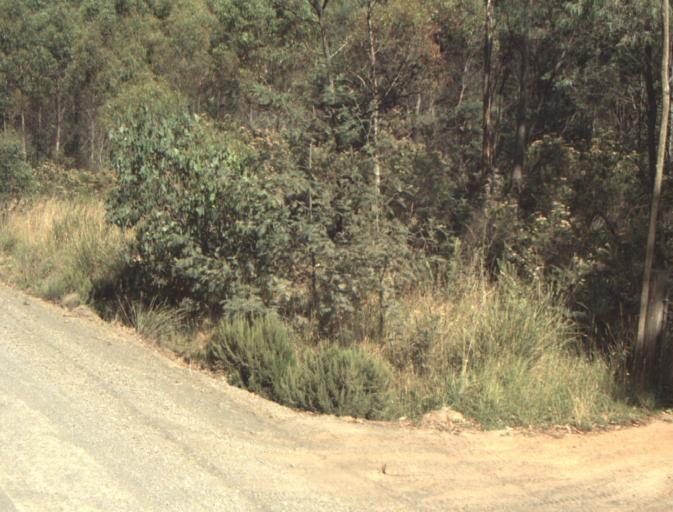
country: AU
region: Tasmania
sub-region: Launceston
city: Newstead
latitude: -41.3646
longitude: 147.2494
